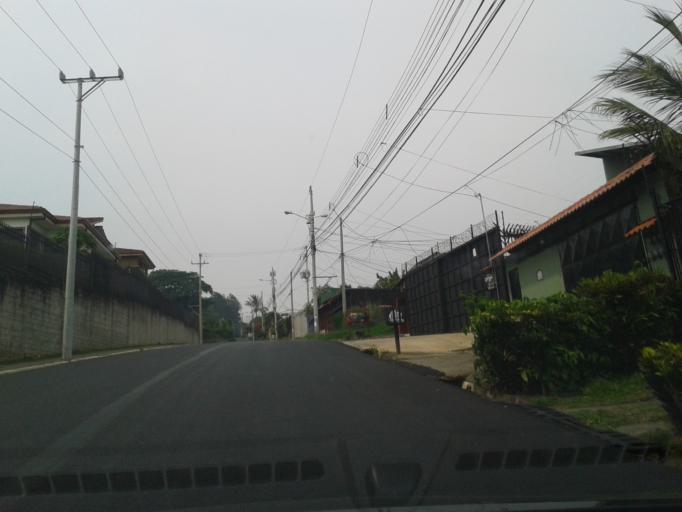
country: CR
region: Heredia
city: San Francisco
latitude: 9.9802
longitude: -84.1354
